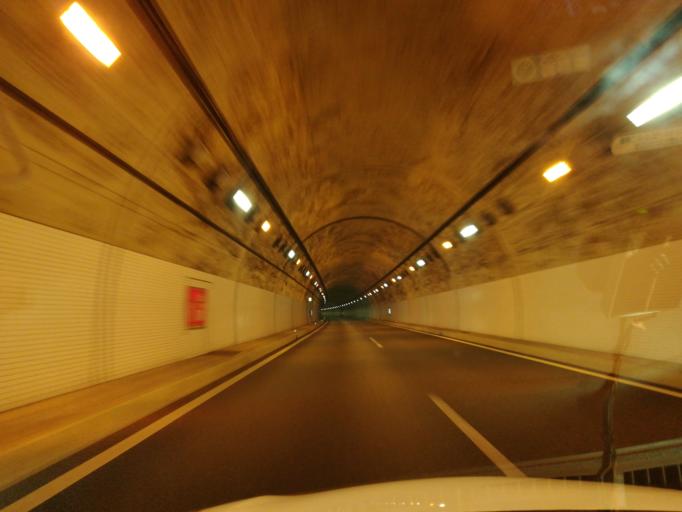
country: JP
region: Kochi
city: Kochi-shi
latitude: 33.6821
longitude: 133.6838
